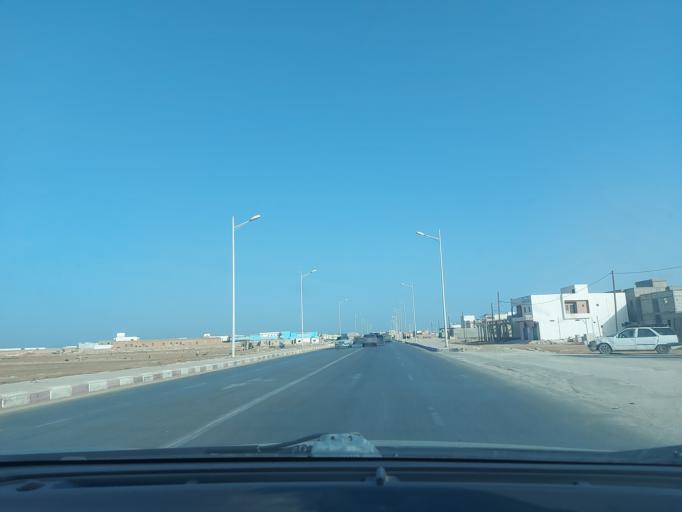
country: MR
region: Nouakchott
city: Nouakchott
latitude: 18.0959
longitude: -16.0168
